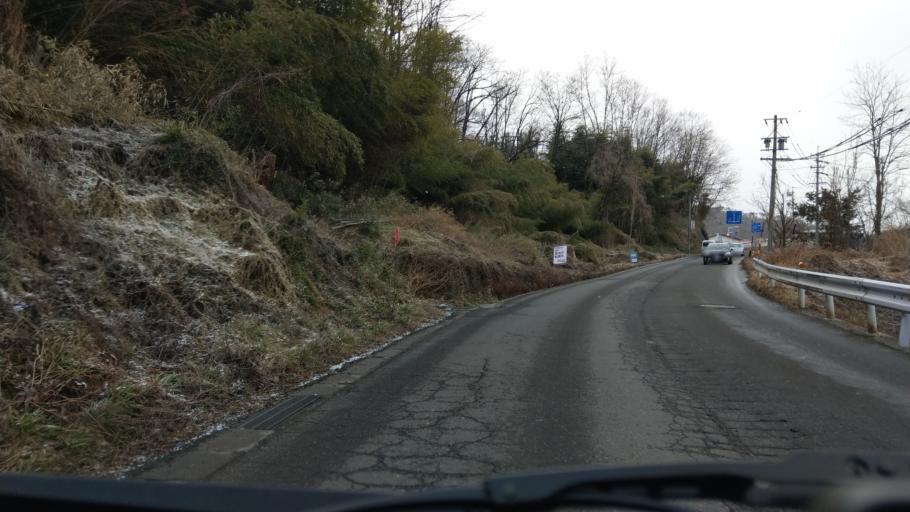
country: JP
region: Nagano
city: Kamimaruko
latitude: 36.3281
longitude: 138.3469
